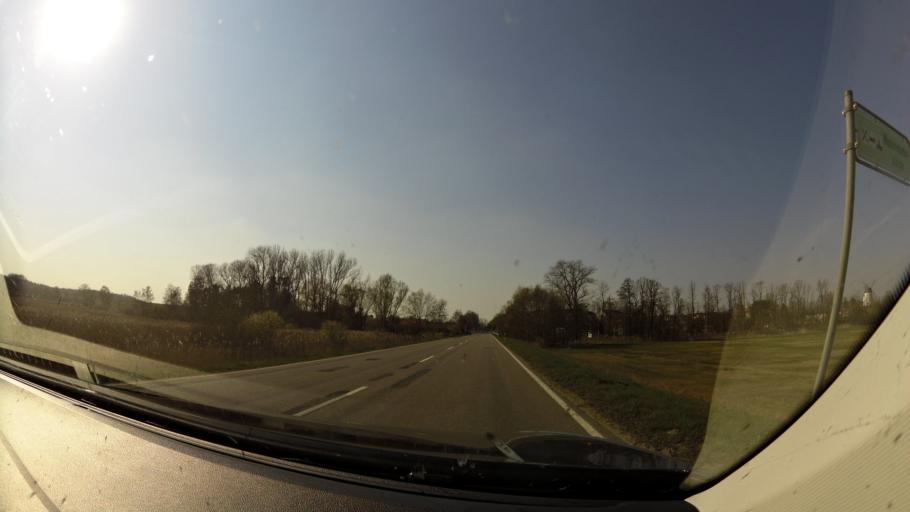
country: DE
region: Mecklenburg-Vorpommern
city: Bad Sulze
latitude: 54.1042
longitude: 12.6673
